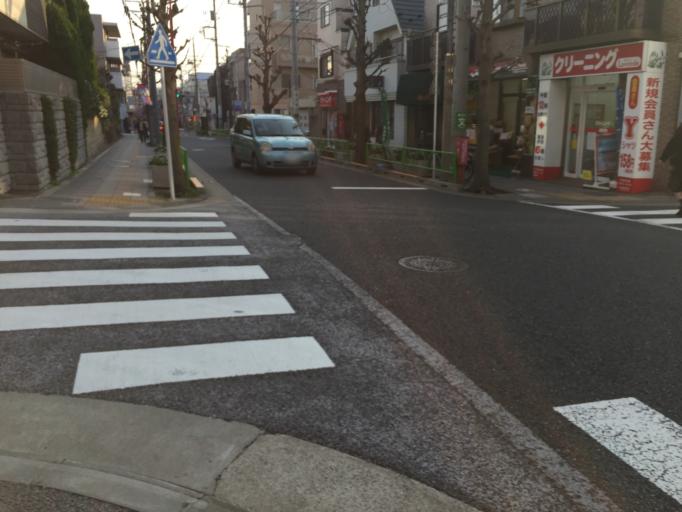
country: JP
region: Tokyo
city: Tokyo
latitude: 35.6085
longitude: 139.6538
